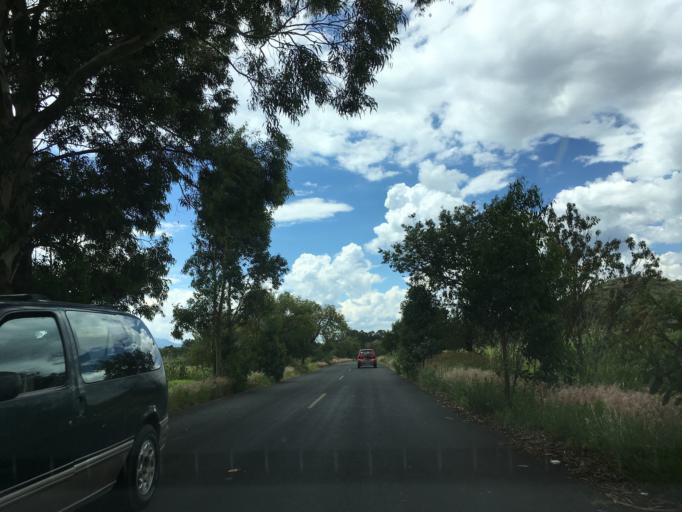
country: MX
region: Michoacan
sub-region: Zacapu
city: Naranja de Tapia
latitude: 19.8172
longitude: -101.7032
